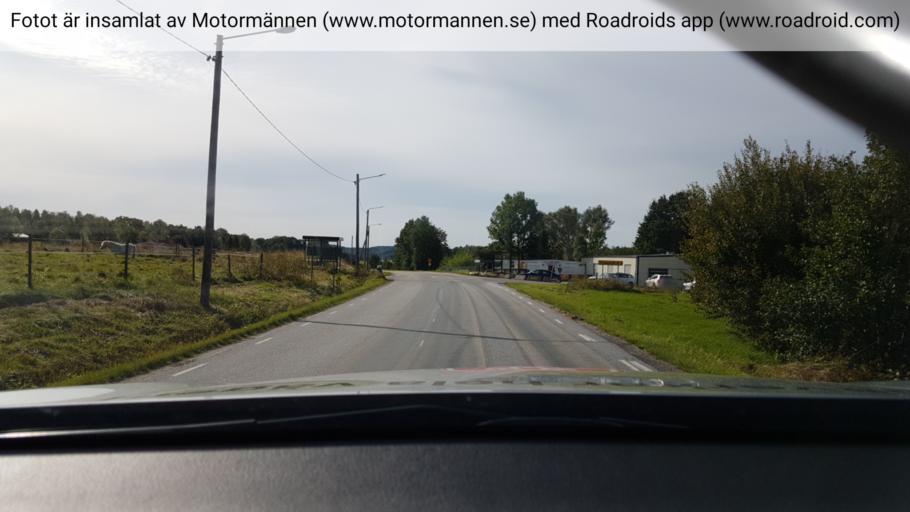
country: SE
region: Vaestra Goetaland
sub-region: Uddevalla Kommun
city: Ljungskile
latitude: 58.2868
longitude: 11.8505
